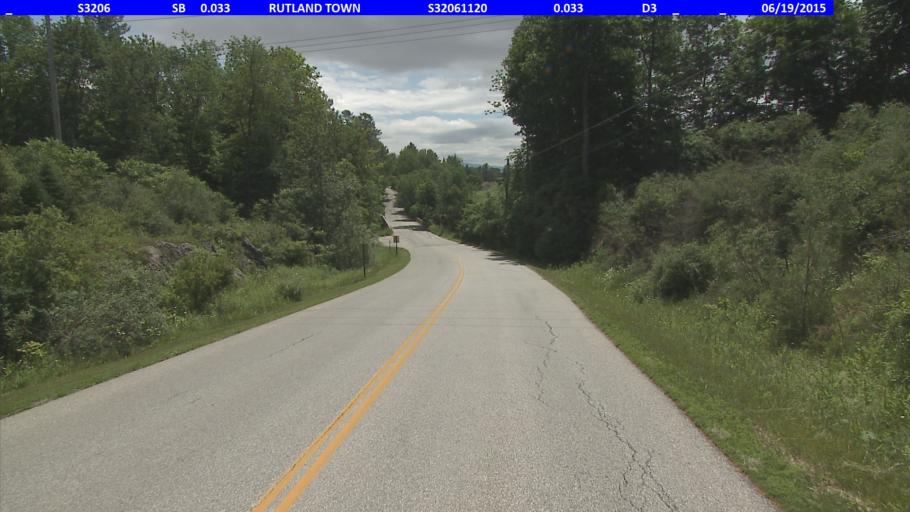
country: US
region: Vermont
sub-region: Rutland County
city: Rutland
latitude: 43.6303
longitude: -72.9886
